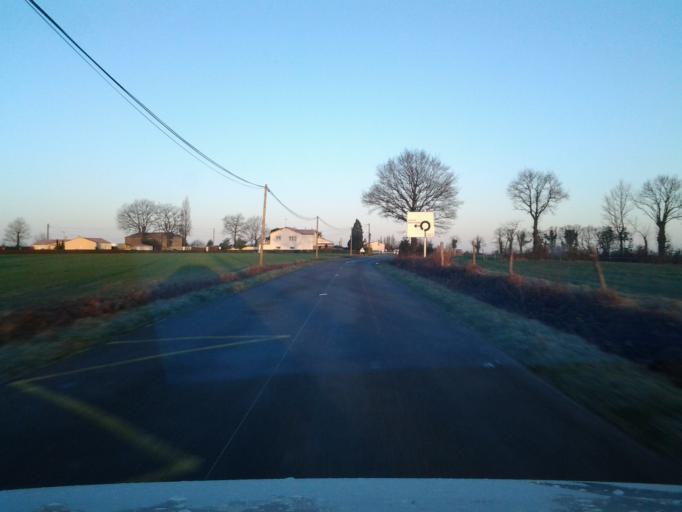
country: FR
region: Pays de la Loire
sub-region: Departement de la Vendee
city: La Gaubretiere
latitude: 46.9318
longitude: -1.0485
